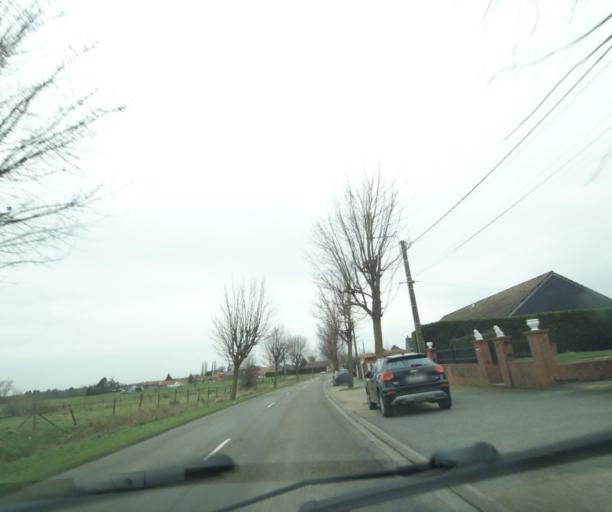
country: FR
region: Nord-Pas-de-Calais
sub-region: Departement du Nord
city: Quarouble
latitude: 50.3821
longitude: 3.6233
